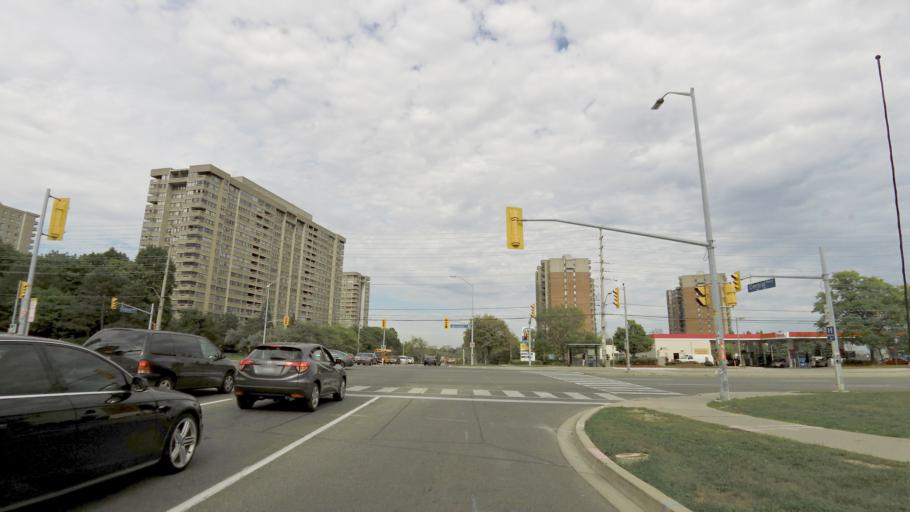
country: CA
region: Ontario
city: Mississauga
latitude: 43.5890
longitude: -79.6293
